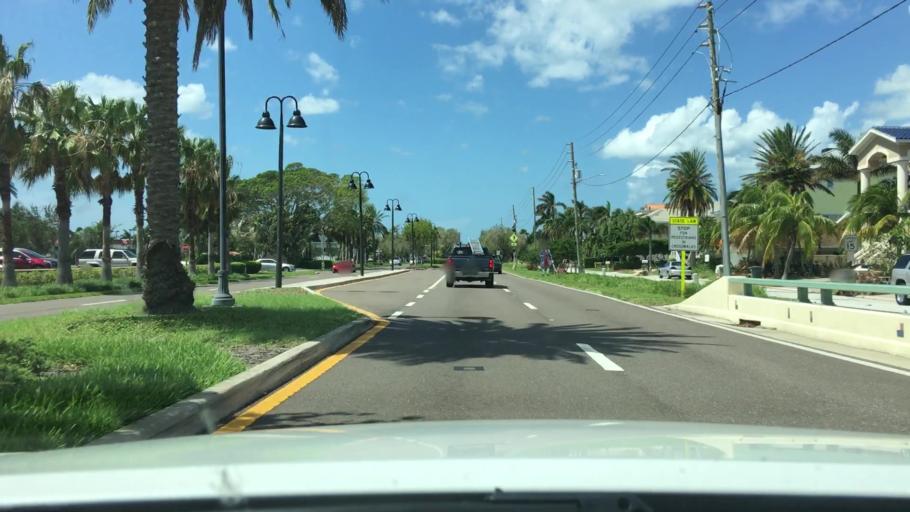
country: US
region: Florida
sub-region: Pinellas County
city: Treasure Island
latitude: 27.7708
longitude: -82.7554
